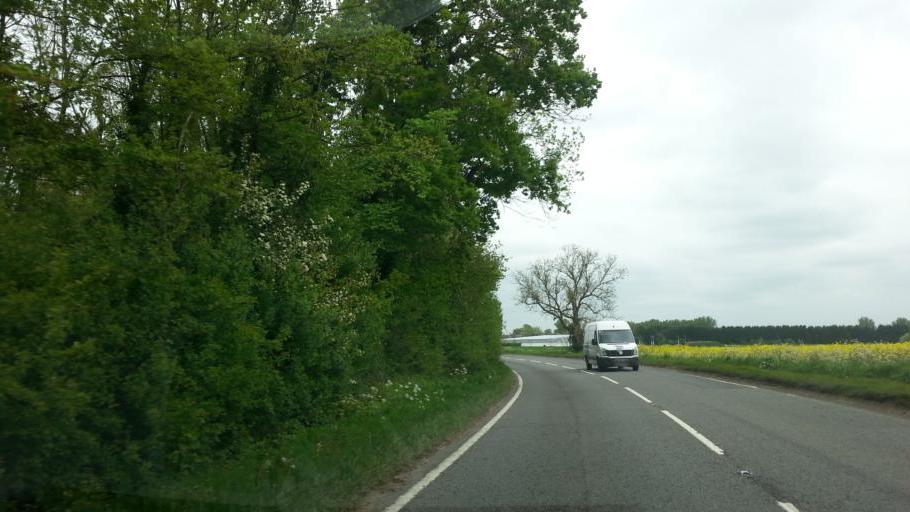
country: GB
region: England
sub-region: Lincolnshire
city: Bourne
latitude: 52.7510
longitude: -0.3702
